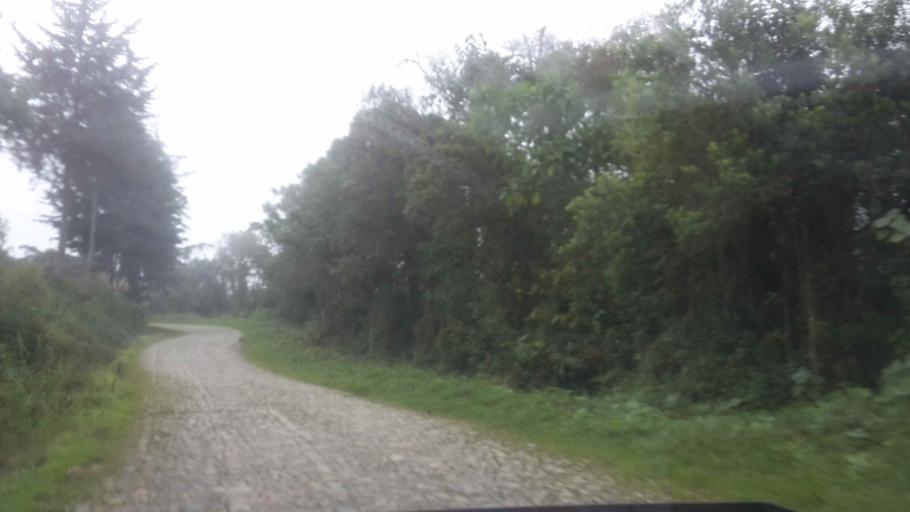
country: BO
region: Cochabamba
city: Colomi
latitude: -17.1297
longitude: -65.9562
